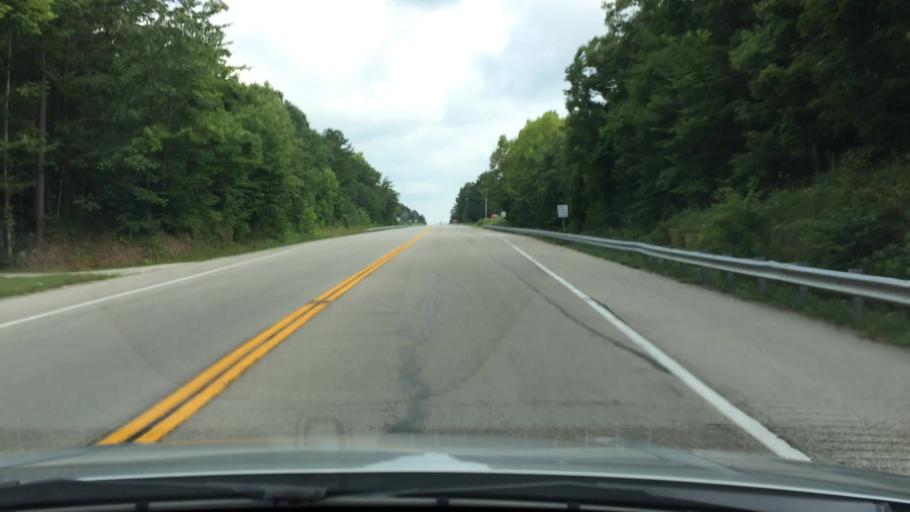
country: US
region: Kentucky
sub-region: Pulaski County
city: Somerset
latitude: 36.9197
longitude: -84.5178
